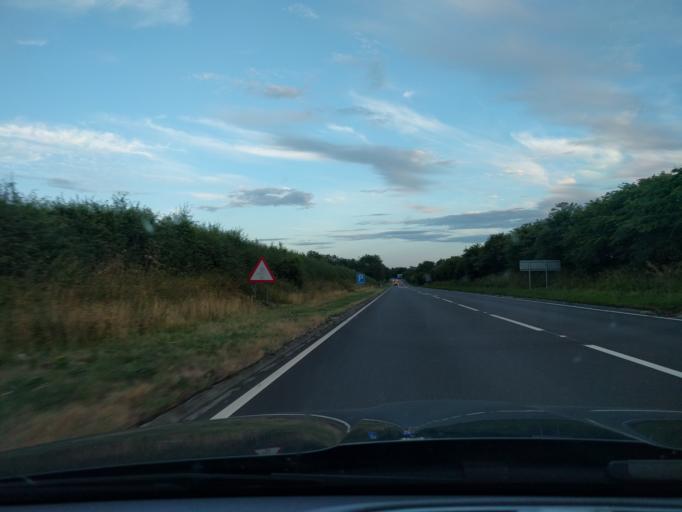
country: GB
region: England
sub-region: Northumberland
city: Felton
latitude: 55.2717
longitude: -1.7230
